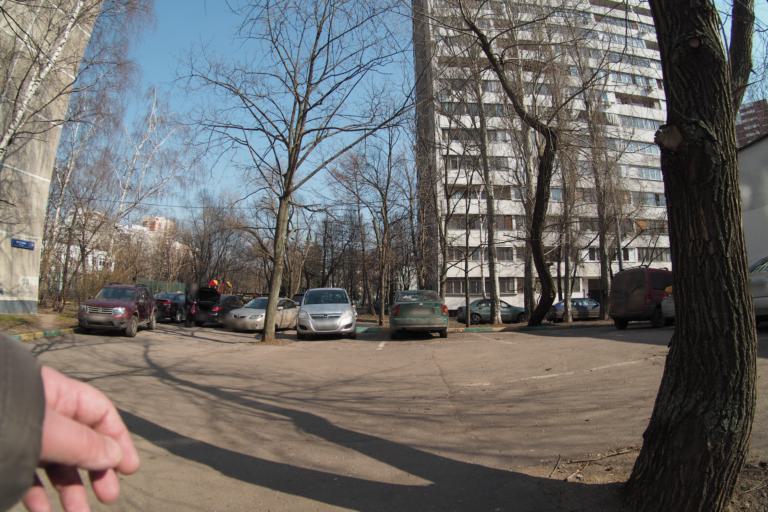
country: RU
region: Moscow
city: Matveyevskoye
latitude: 55.7108
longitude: 37.4824
